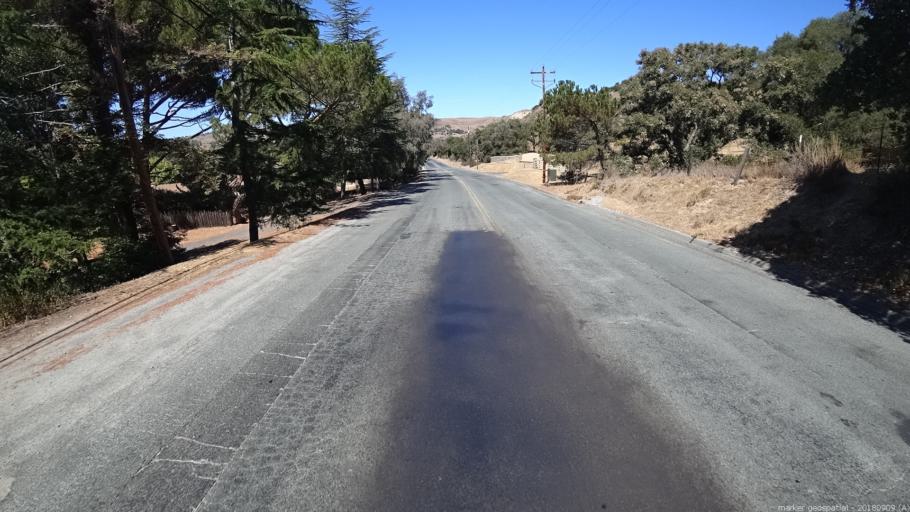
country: US
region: California
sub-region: Monterey County
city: Carmel Valley Village
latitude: 36.5743
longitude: -121.7136
